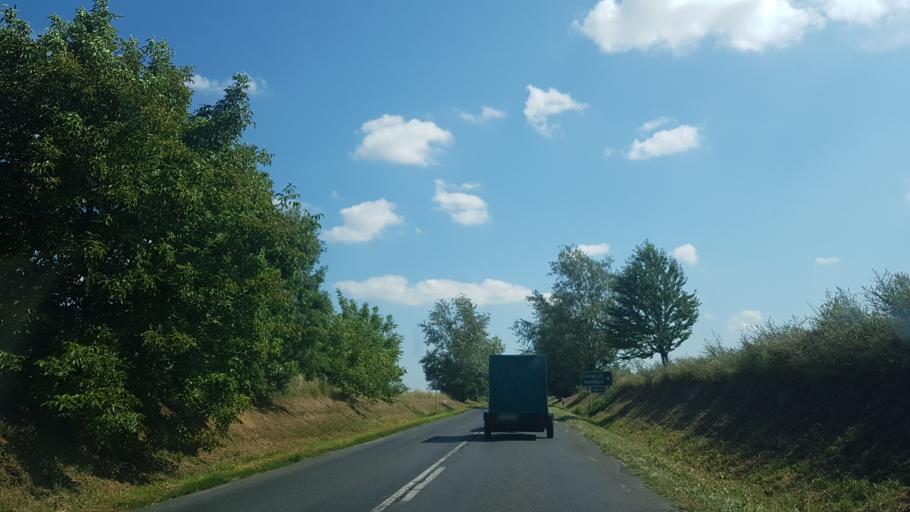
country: HU
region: Somogy
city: Bohonye
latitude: 46.4511
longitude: 17.3725
